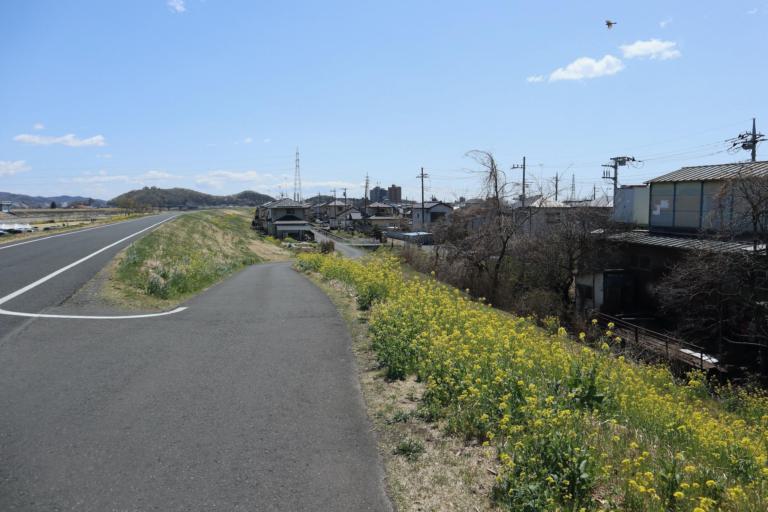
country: JP
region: Tochigi
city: Ashikaga
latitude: 36.3357
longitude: 139.4199
